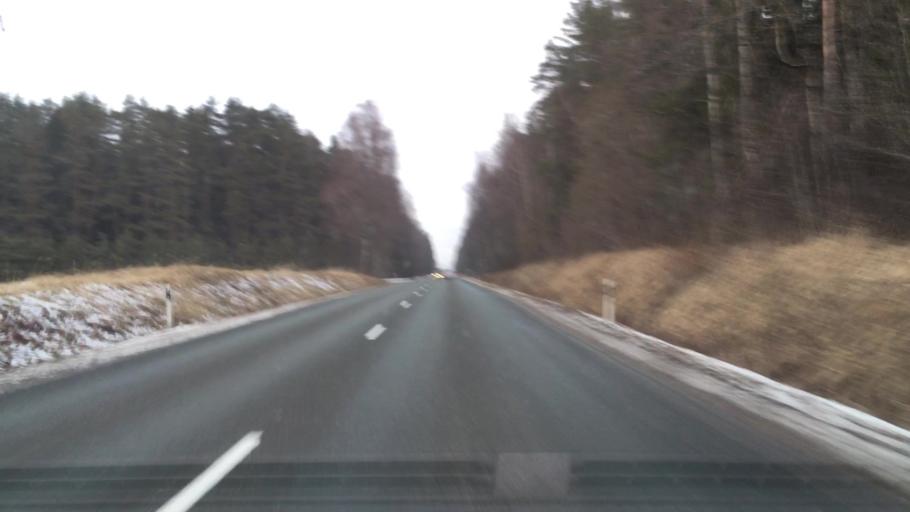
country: LV
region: Valmieras Rajons
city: Valmiera
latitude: 57.4983
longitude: 25.4172
